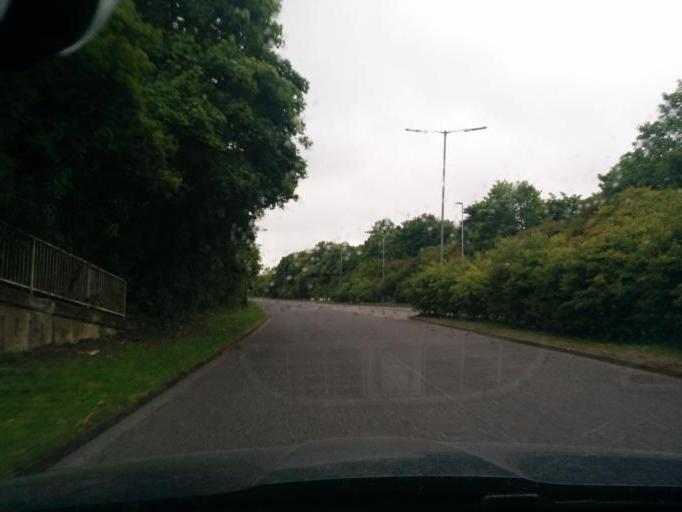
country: GB
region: England
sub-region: Northumberland
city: Cramlington
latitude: 55.0945
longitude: -1.6112
